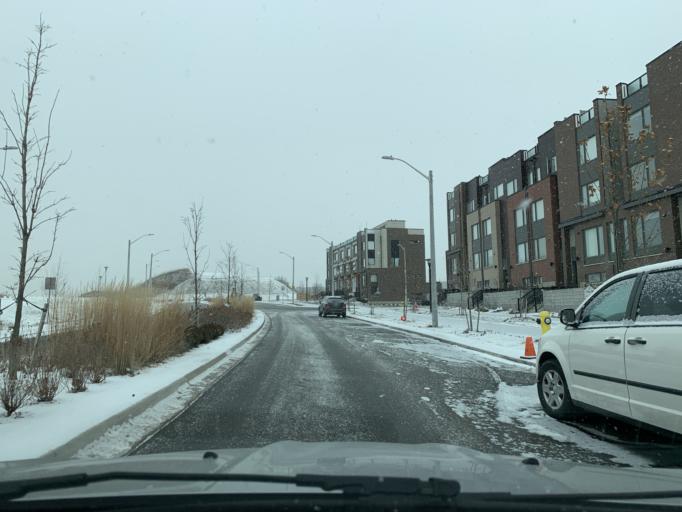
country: CA
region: Ontario
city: Concord
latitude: 43.7373
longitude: -79.4772
